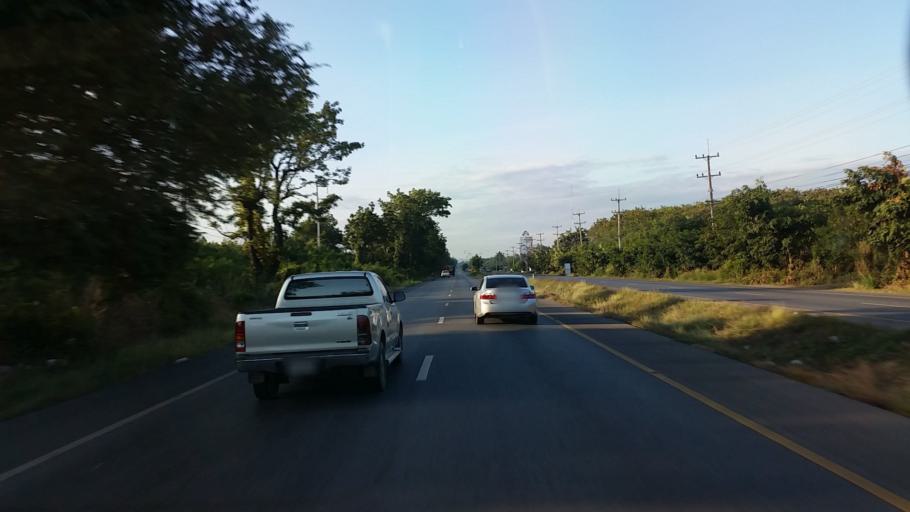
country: TH
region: Lop Buri
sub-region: Amphoe Tha Luang
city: Tha Luang
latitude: 15.1114
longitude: 101.0269
